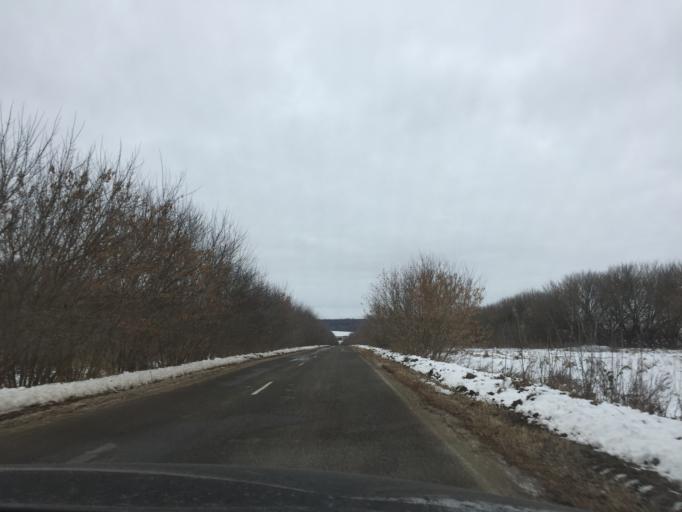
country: RU
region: Tula
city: Teploye
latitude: 53.7811
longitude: 37.6291
